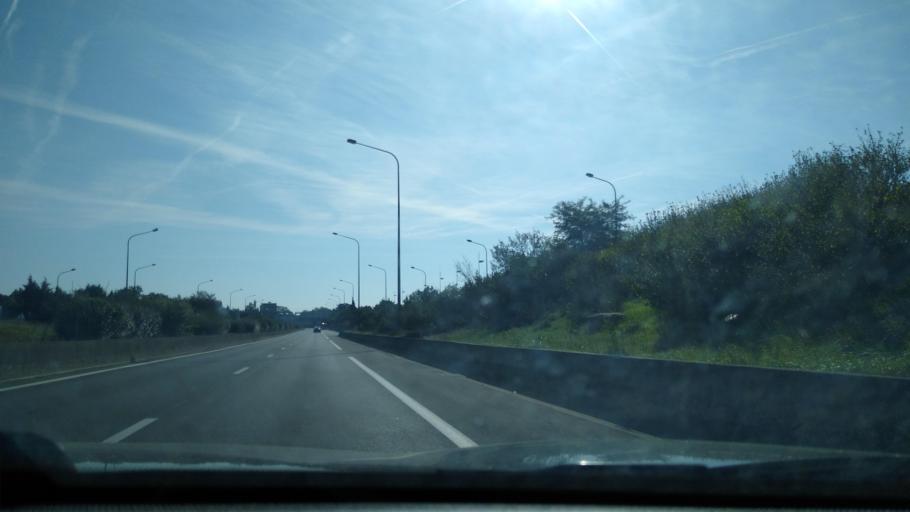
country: FR
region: Midi-Pyrenees
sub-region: Departement de la Haute-Garonne
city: Colomiers
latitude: 43.5969
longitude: 1.3634
